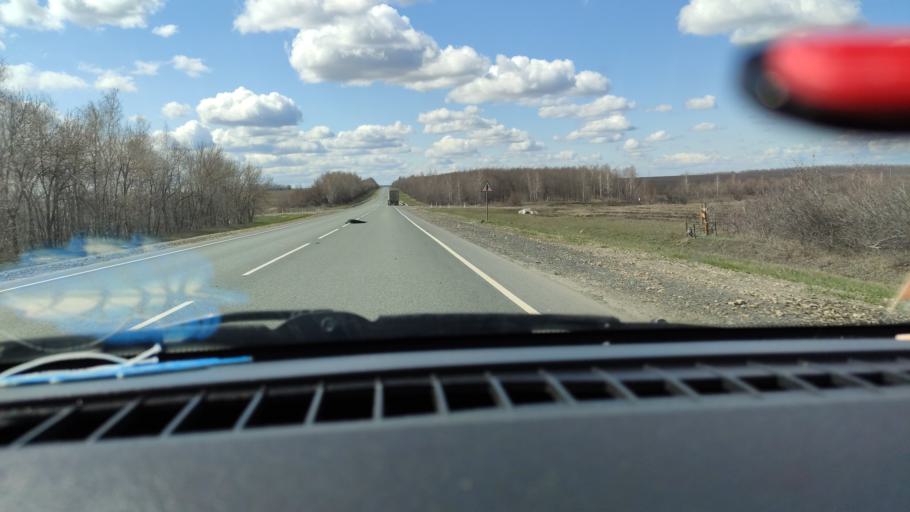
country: RU
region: Saratov
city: Khvalynsk
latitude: 52.6053
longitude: 48.1508
